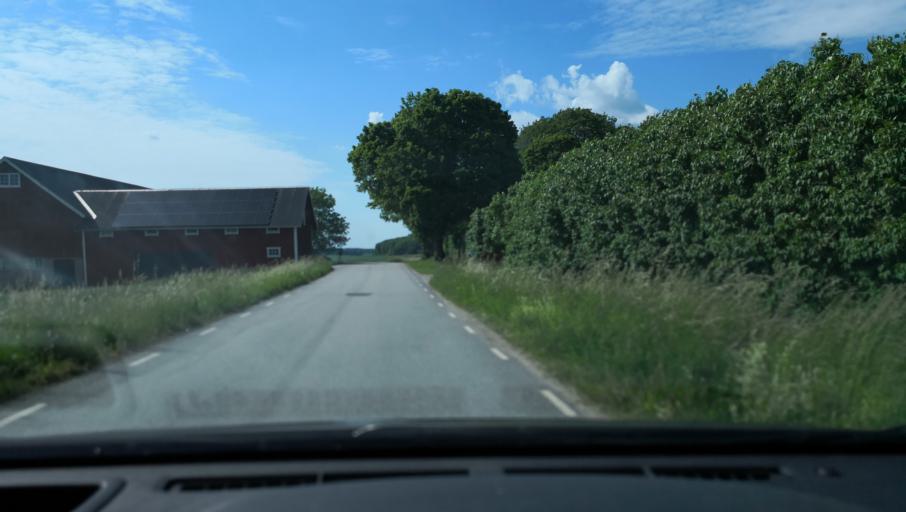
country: SE
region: Uppsala
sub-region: Enkopings Kommun
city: Orsundsbro
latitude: 59.8163
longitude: 17.3366
